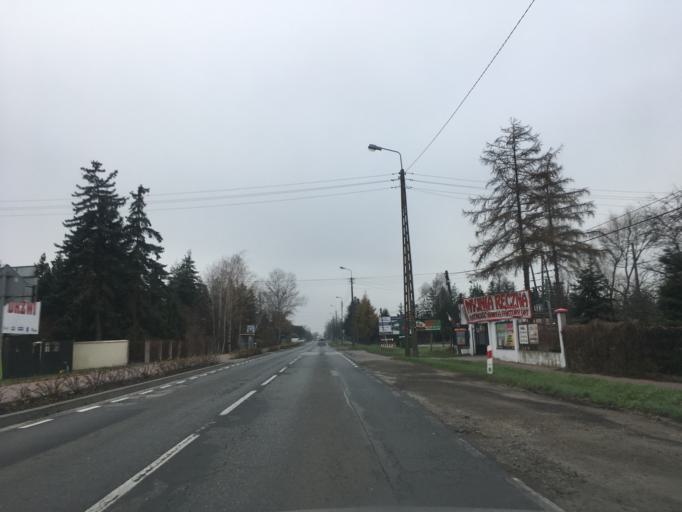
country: PL
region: Masovian Voivodeship
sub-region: Powiat piaseczynski
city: Piaseczno
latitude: 52.0822
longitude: 20.9936
